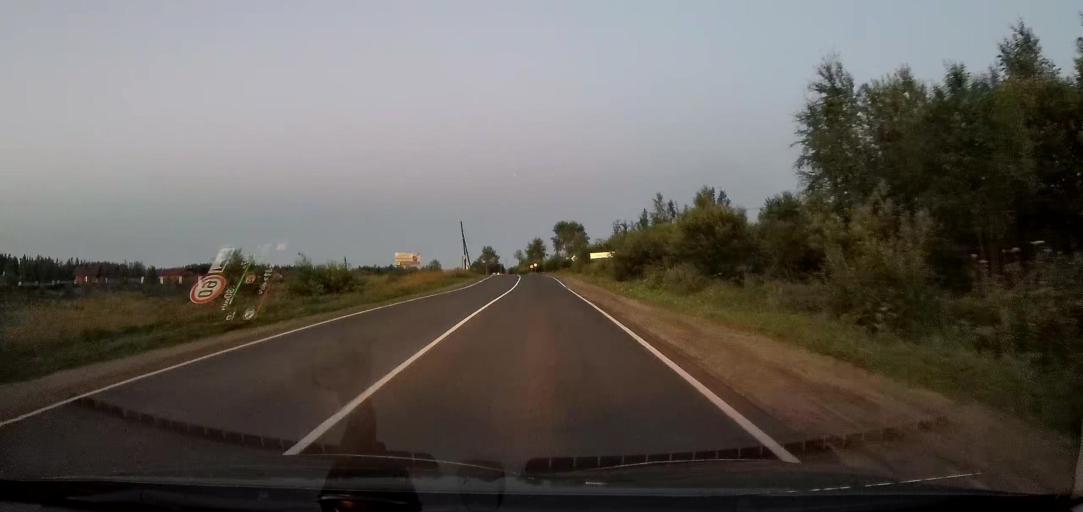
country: RU
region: Arkhangelskaya
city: Uyemskiy
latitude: 64.4481
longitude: 40.9459
